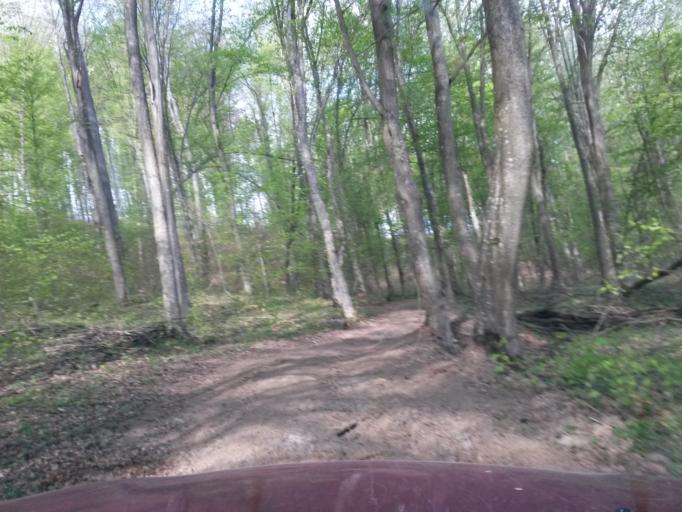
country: SK
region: Presovsky
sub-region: Okres Presov
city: Presov
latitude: 48.9473
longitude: 21.1411
